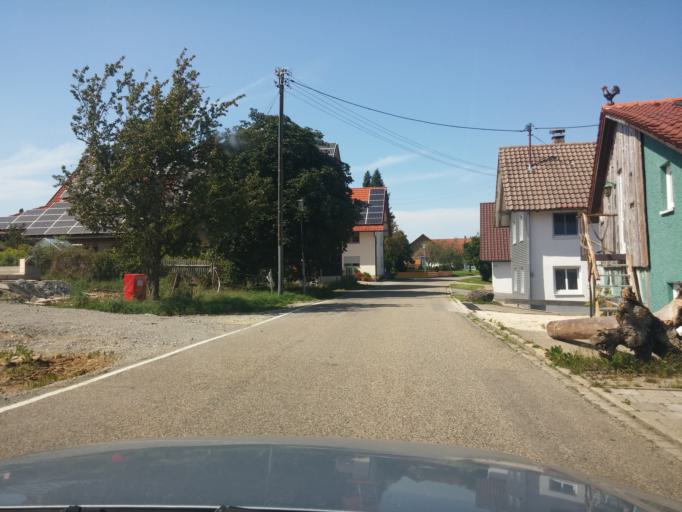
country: DE
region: Baden-Wuerttemberg
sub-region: Tuebingen Region
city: Aichstetten
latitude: 47.8610
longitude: 10.0673
